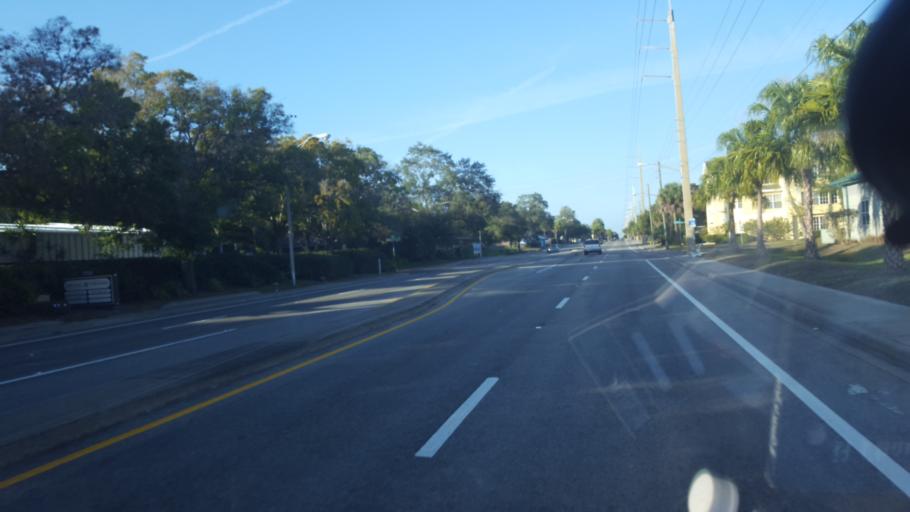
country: US
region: Florida
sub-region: Sarasota County
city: Southgate
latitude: 27.3173
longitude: -82.5140
